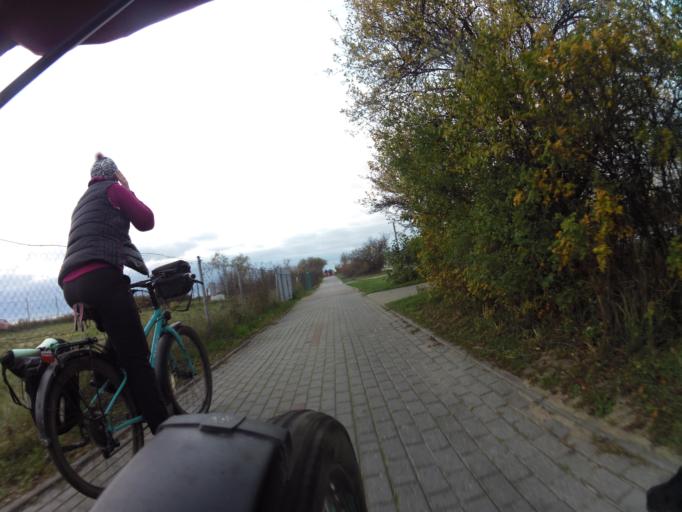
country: PL
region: Pomeranian Voivodeship
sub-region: Powiat pucki
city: Jastarnia
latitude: 54.7289
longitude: 18.5951
